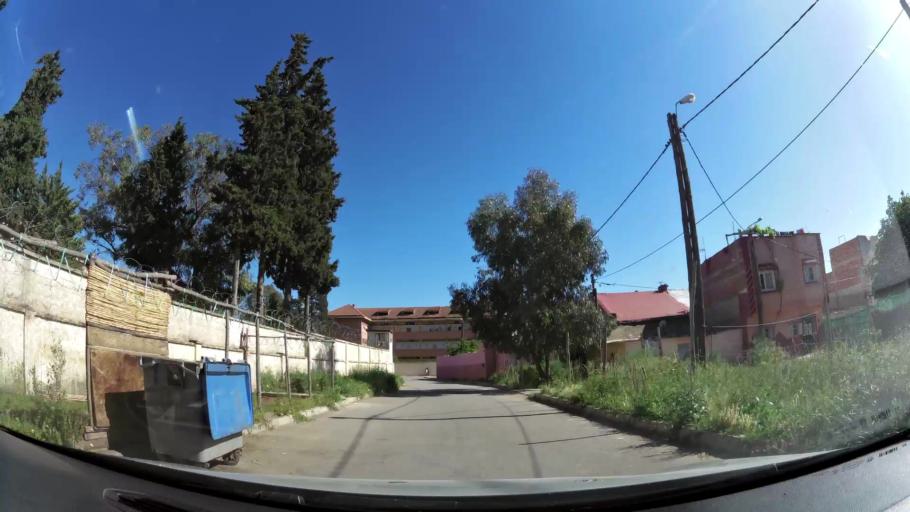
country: MA
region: Meknes-Tafilalet
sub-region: Meknes
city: Meknes
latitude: 33.8887
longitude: -5.5290
